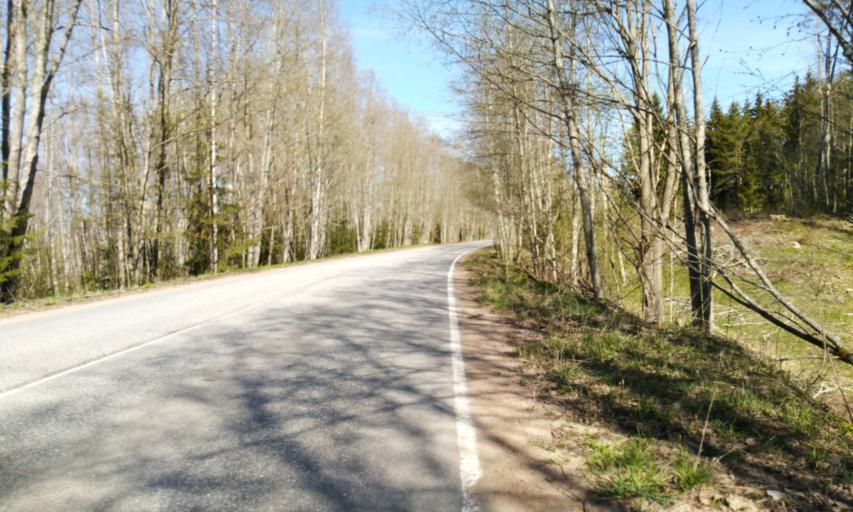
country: RU
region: Leningrad
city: Garbolovo
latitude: 60.4097
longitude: 30.4600
